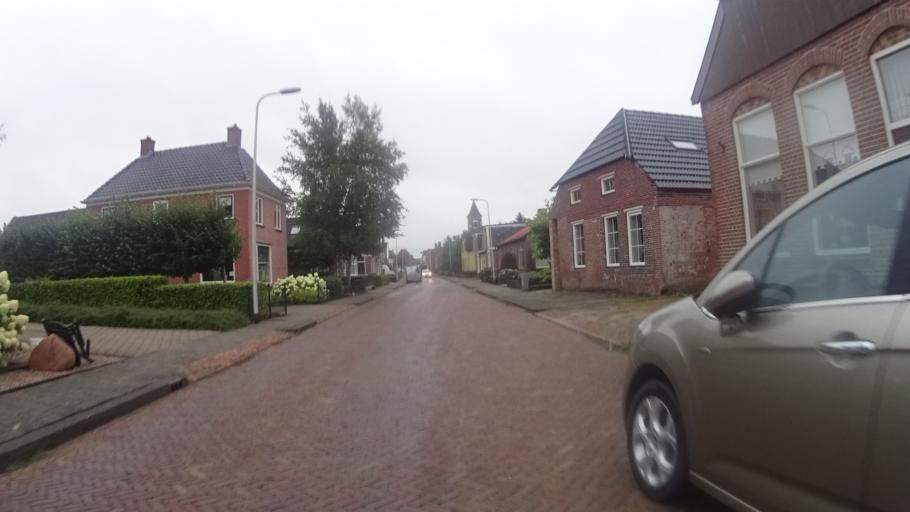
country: NL
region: Groningen
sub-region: Gemeente  Oldambt
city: Winschoten
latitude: 53.1792
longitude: 6.9679
